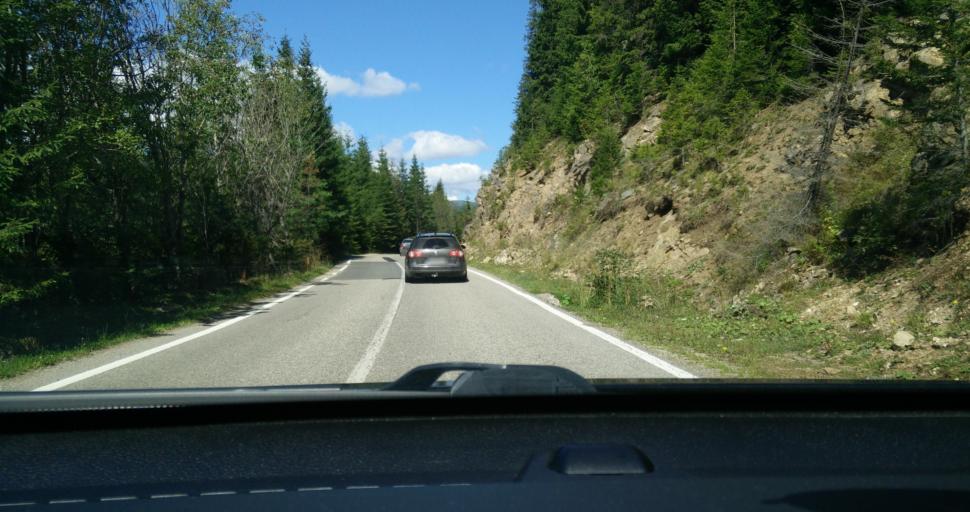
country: RO
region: Alba
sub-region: Comuna Sugag
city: Sugag
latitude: 45.5453
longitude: 23.6364
